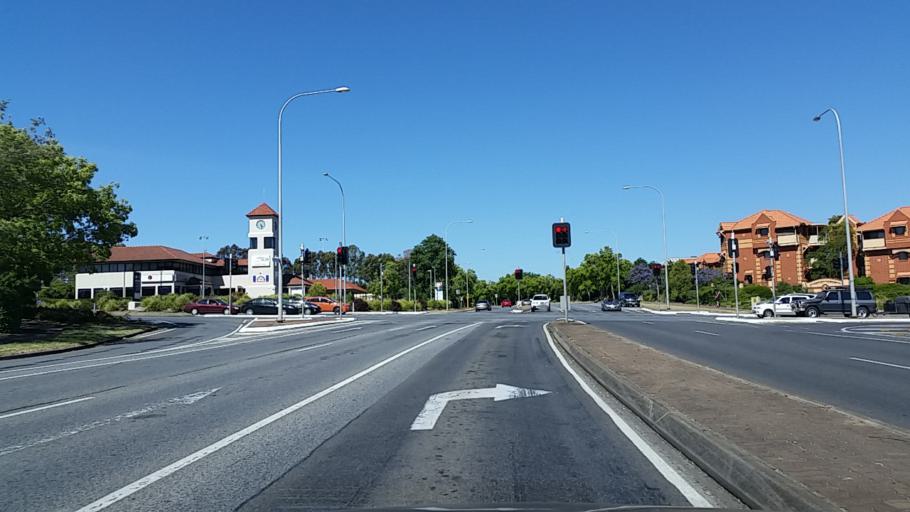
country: AU
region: South Australia
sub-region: Tea Tree Gully
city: Golden Grove
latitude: -34.7906
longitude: 138.6968
